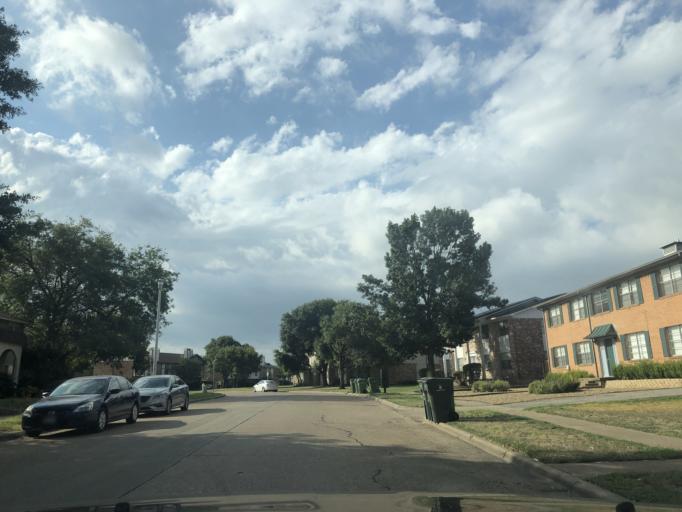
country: US
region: Texas
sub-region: Dallas County
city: Garland
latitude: 32.8834
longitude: -96.6607
